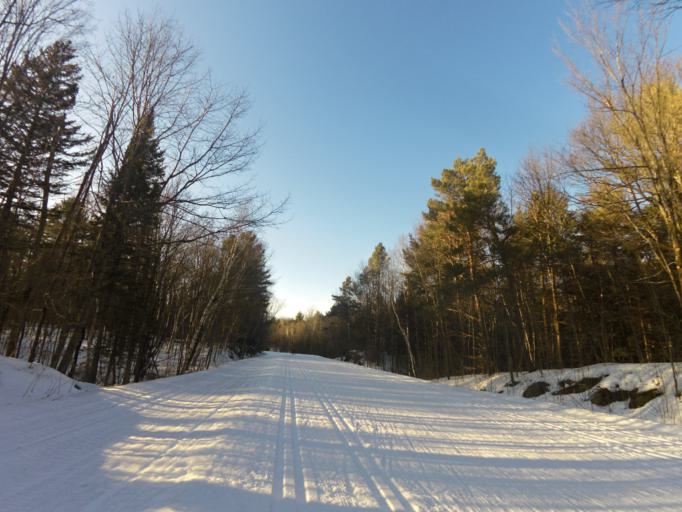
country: CA
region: Quebec
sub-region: Outaouais
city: Gatineau
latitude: 45.5234
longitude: -75.8340
